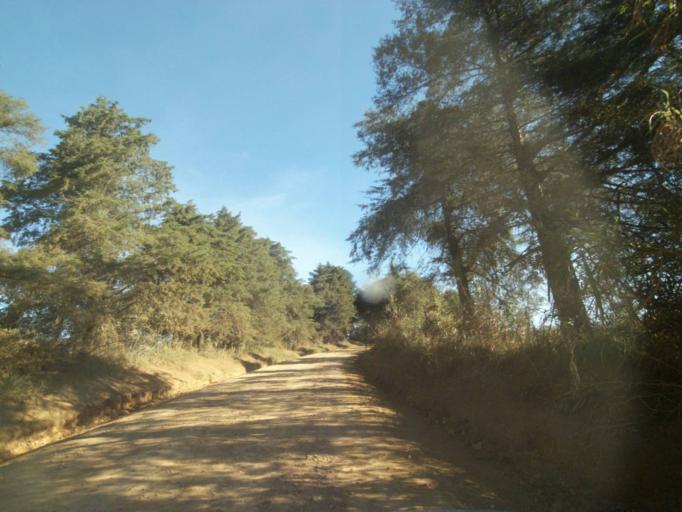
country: BR
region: Parana
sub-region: Tibagi
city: Tibagi
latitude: -24.5274
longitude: -50.5104
